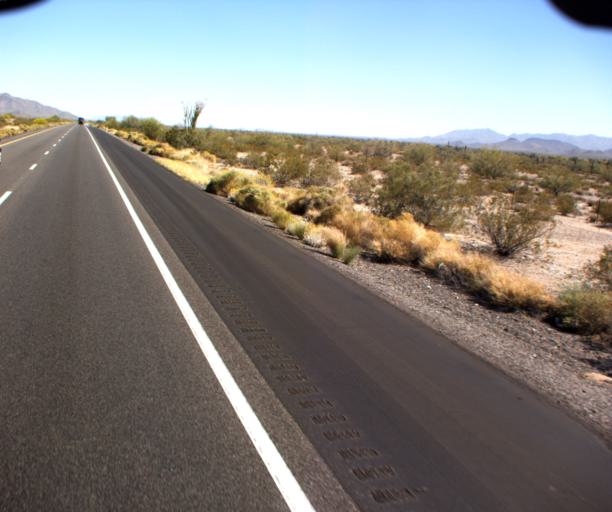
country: US
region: Arizona
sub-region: Maricopa County
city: Gila Bend
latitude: 32.8897
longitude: -112.4820
